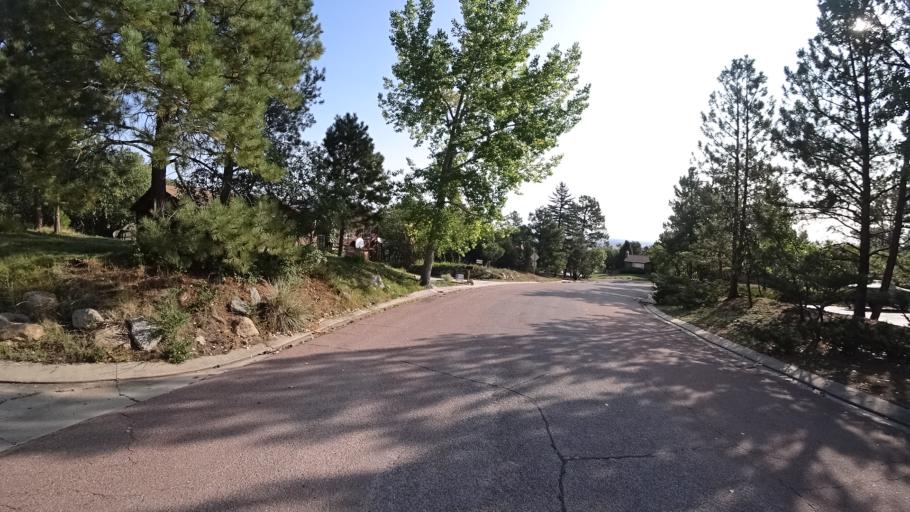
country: US
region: Colorado
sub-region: El Paso County
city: Colorado Springs
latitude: 38.8202
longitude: -104.8698
